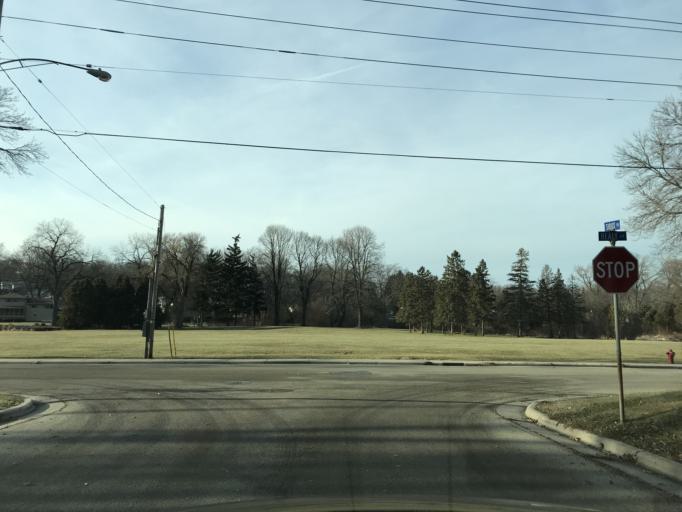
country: US
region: Wisconsin
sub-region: Dane County
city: Monona
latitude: 43.0608
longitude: -89.3434
